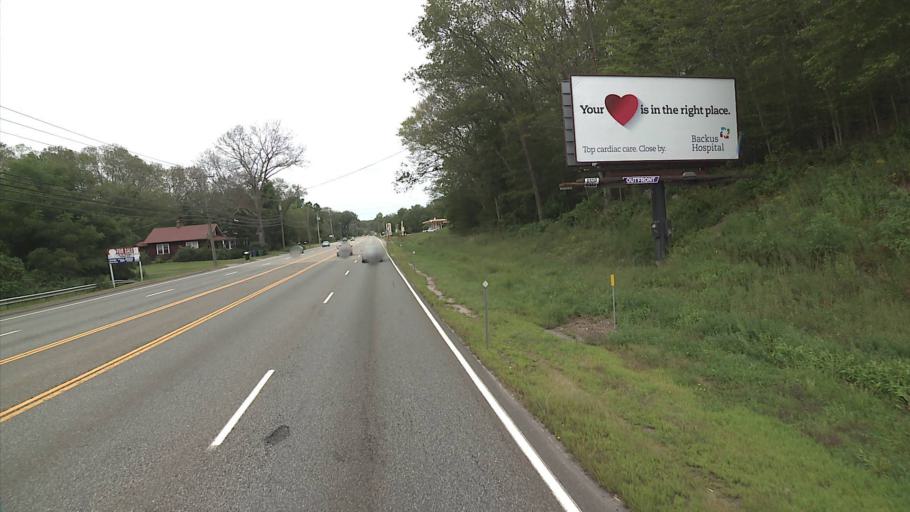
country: US
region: Connecticut
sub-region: New London County
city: Central Waterford
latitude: 41.3855
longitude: -72.1580
